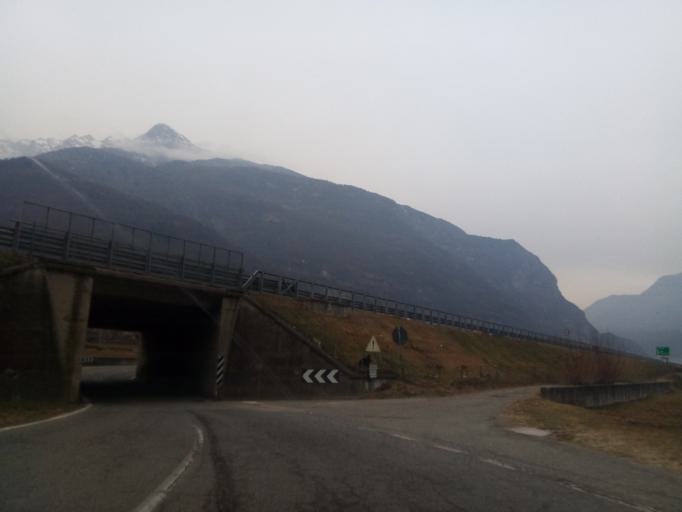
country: IT
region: Piedmont
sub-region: Provincia di Torino
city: Tavagnasco
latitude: 45.5545
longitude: 7.8197
